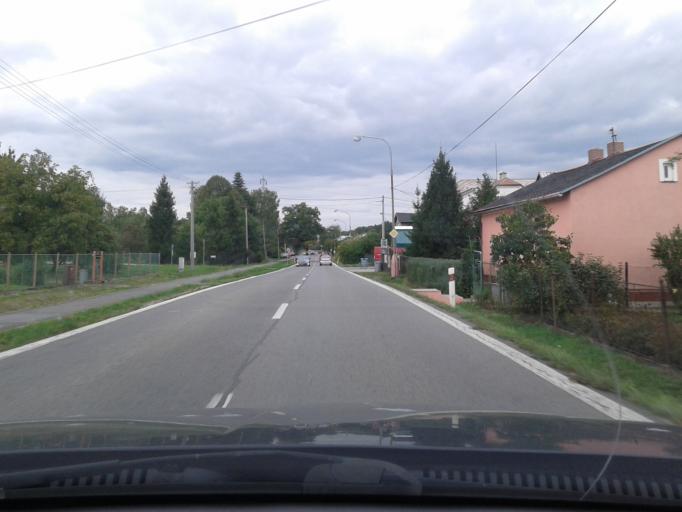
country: CZ
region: Moravskoslezsky
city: Orlova
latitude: 49.8628
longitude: 18.4443
